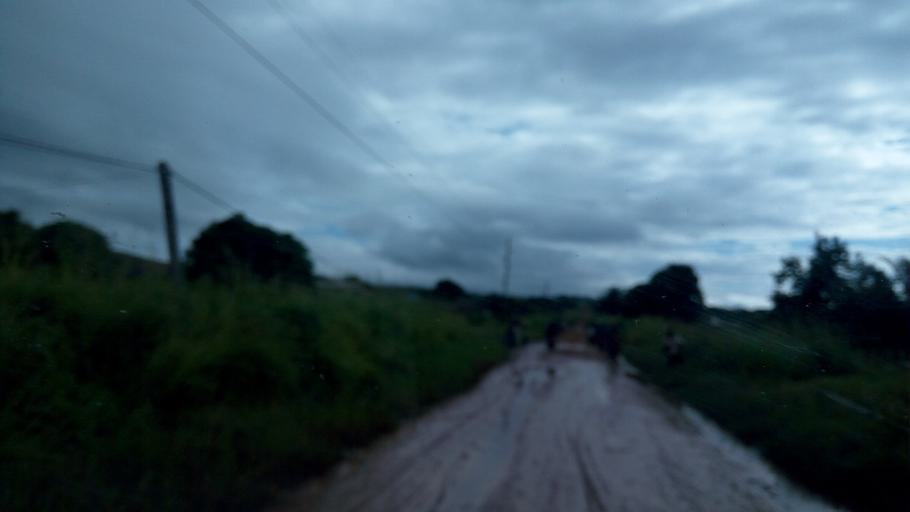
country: ZM
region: Northern
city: Kaputa
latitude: -8.4563
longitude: 28.9047
